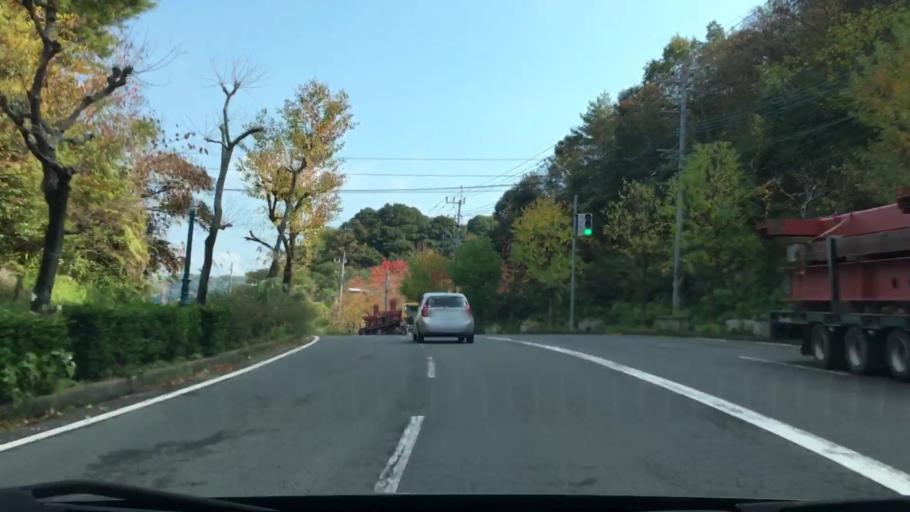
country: JP
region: Nagasaki
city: Sasebo
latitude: 32.9941
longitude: 129.7557
